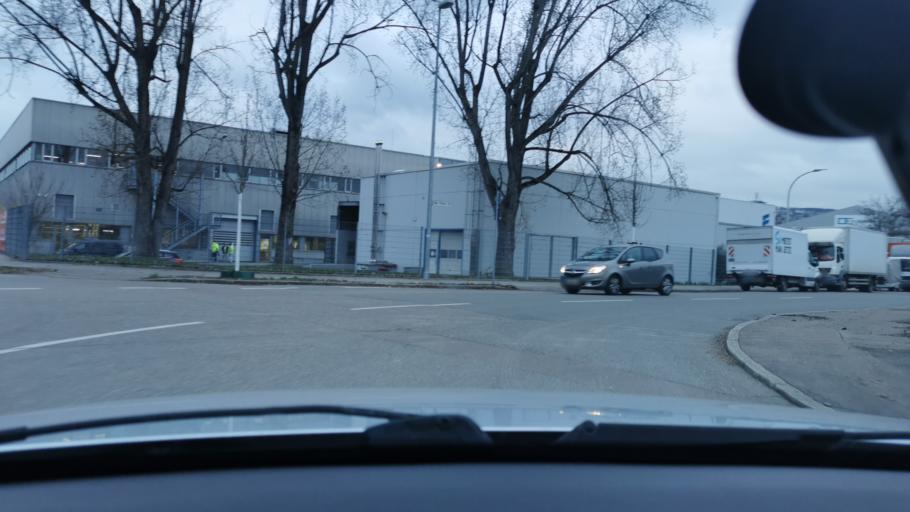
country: DE
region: Baden-Wuerttemberg
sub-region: Regierungsbezirk Stuttgart
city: Denkendorf
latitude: 48.7233
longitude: 9.3397
